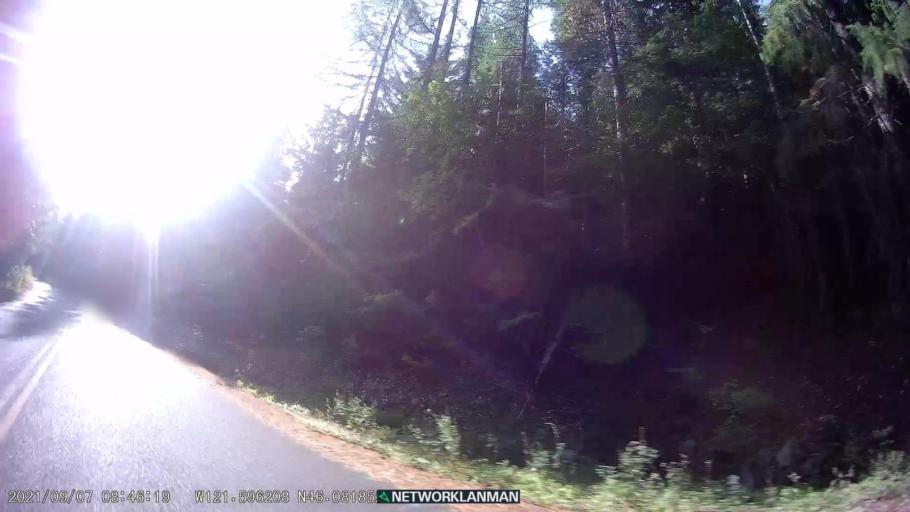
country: US
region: Washington
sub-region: Klickitat County
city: White Salmon
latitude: 46.0818
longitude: -121.5961
